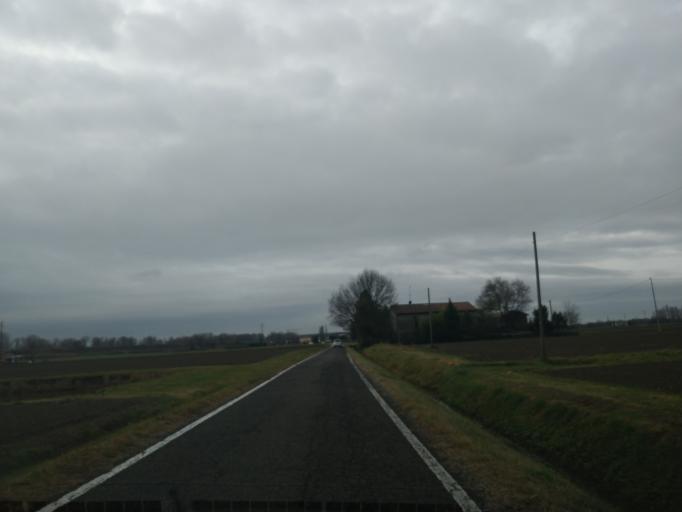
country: IT
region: Emilia-Romagna
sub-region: Provincia di Ferrara
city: Corpo Reno
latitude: 44.7529
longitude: 11.3215
